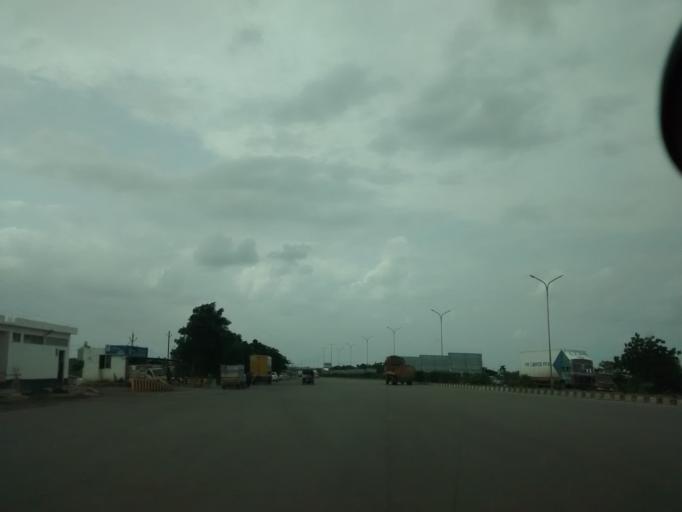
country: IN
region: Telangana
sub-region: Mahbubnagar
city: Alampur
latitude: 15.8882
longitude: 78.0168
